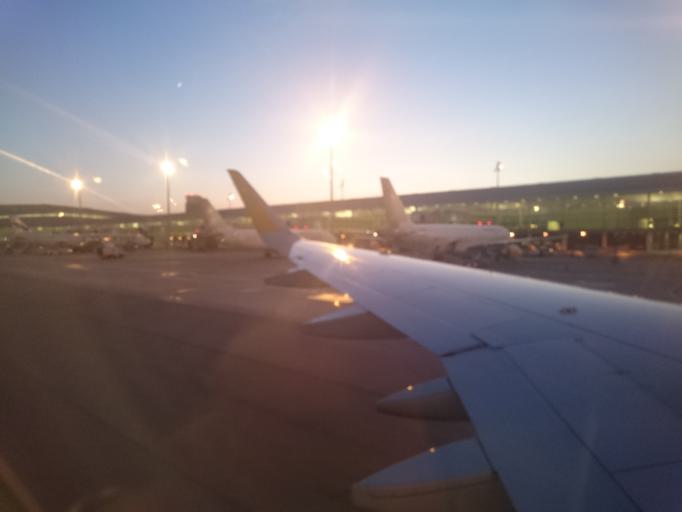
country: ES
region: Catalonia
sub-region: Provincia de Barcelona
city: El Prat de Llobregat
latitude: 41.2900
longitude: 2.0812
